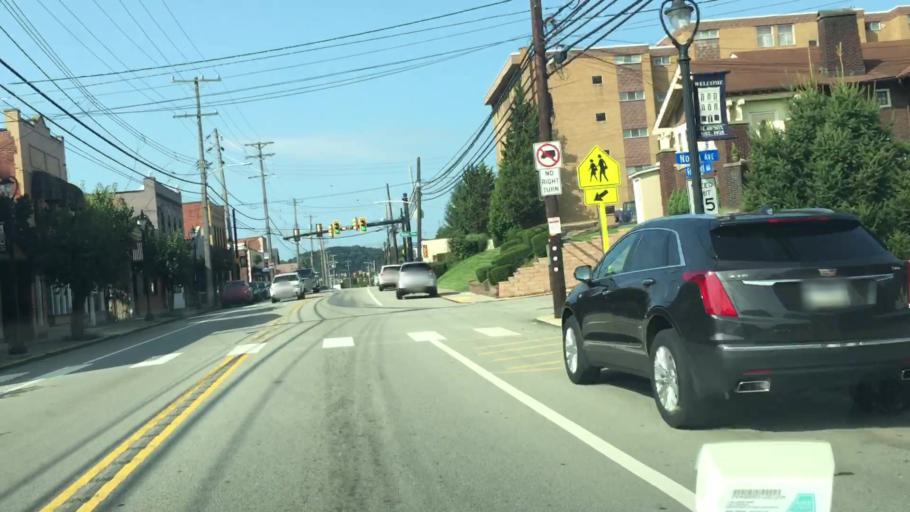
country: US
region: Pennsylvania
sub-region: Allegheny County
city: Blawnox
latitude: 40.4934
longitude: -79.8622
